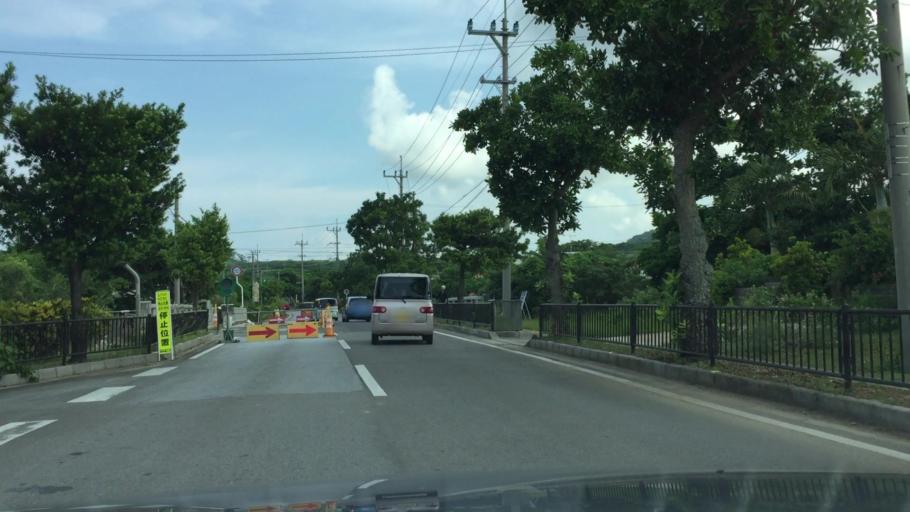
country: JP
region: Okinawa
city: Ishigaki
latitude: 24.4553
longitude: 124.2484
